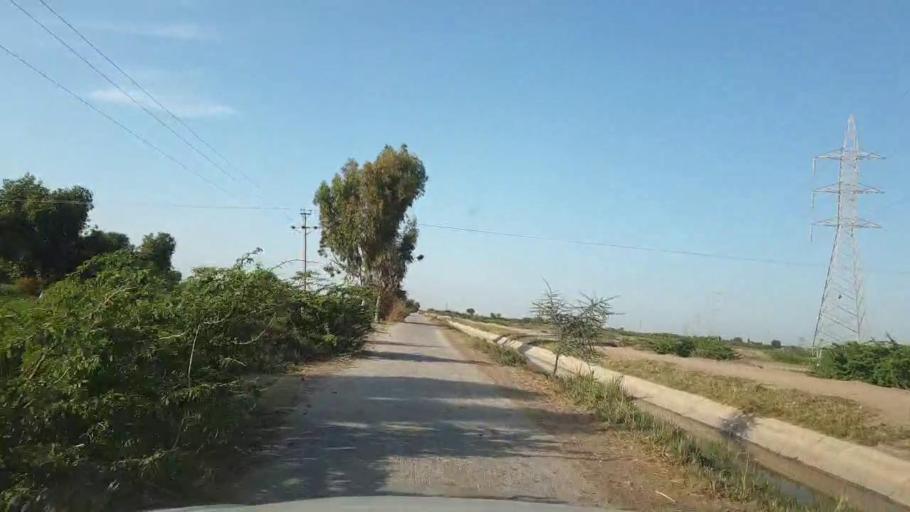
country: PK
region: Sindh
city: Kunri
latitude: 25.0883
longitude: 69.4293
